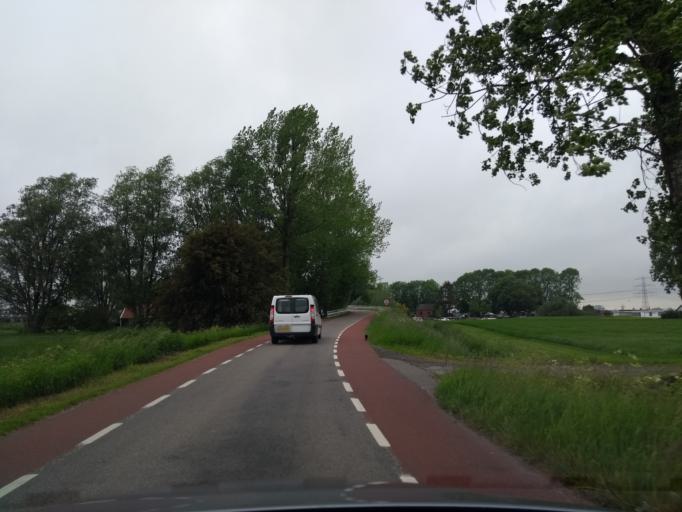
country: NL
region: Groningen
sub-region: Gemeente Zuidhorn
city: Aduard
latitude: 53.2615
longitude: 6.4853
